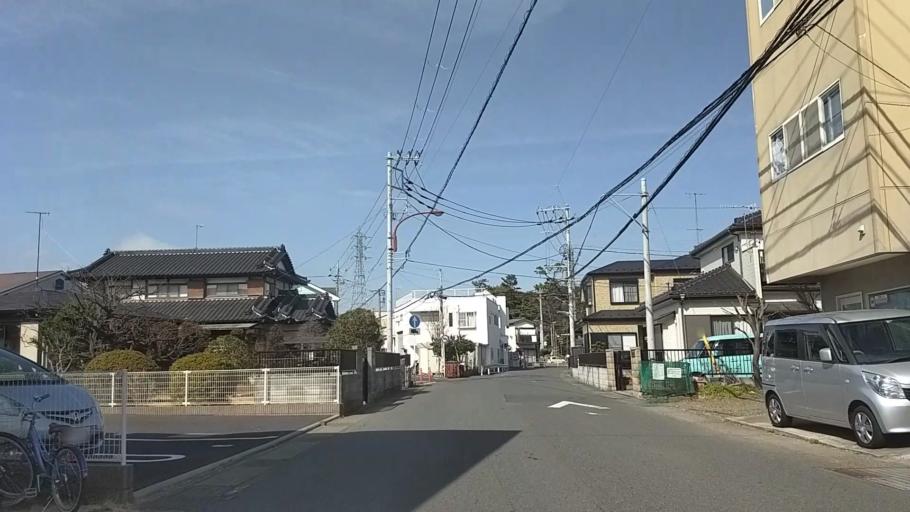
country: JP
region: Kanagawa
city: Chigasaki
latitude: 35.3690
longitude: 139.3811
